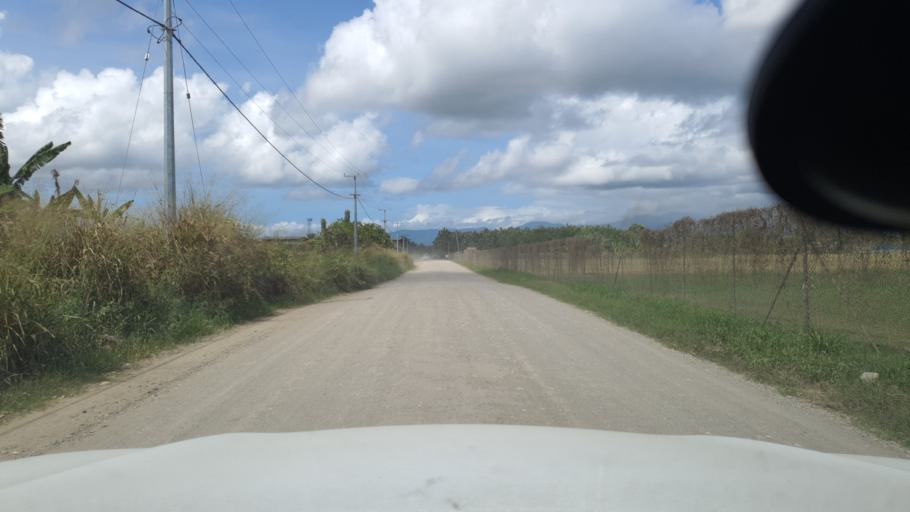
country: SB
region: Guadalcanal
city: Honiara
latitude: -9.4229
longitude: 160.0368
